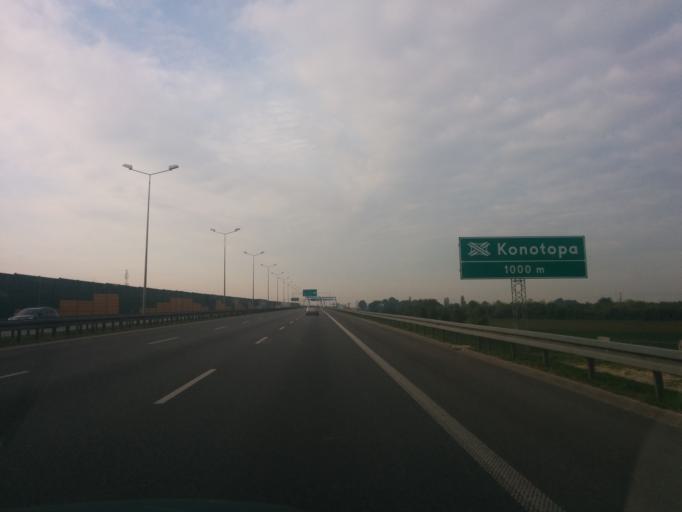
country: PL
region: Masovian Voivodeship
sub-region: Warszawa
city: Ursus
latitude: 52.2125
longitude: 20.8590
